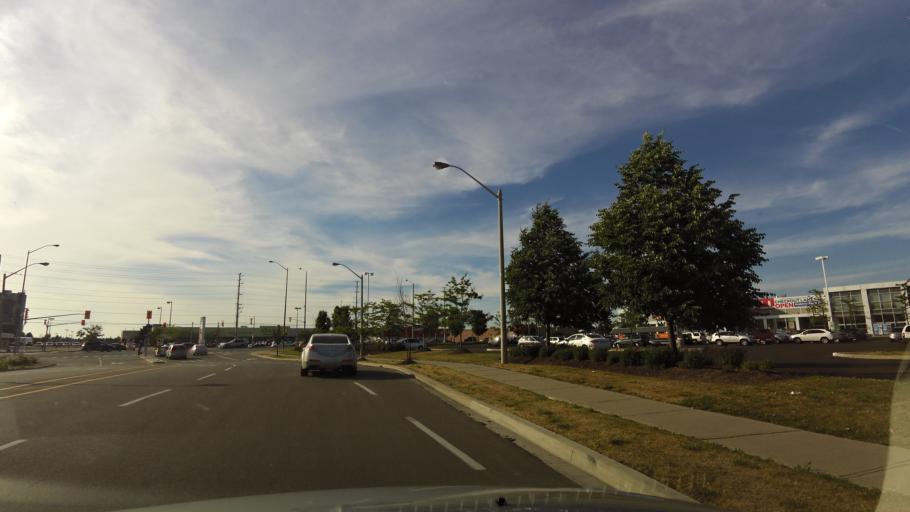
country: CA
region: Ontario
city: Brampton
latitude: 43.6630
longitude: -79.7348
